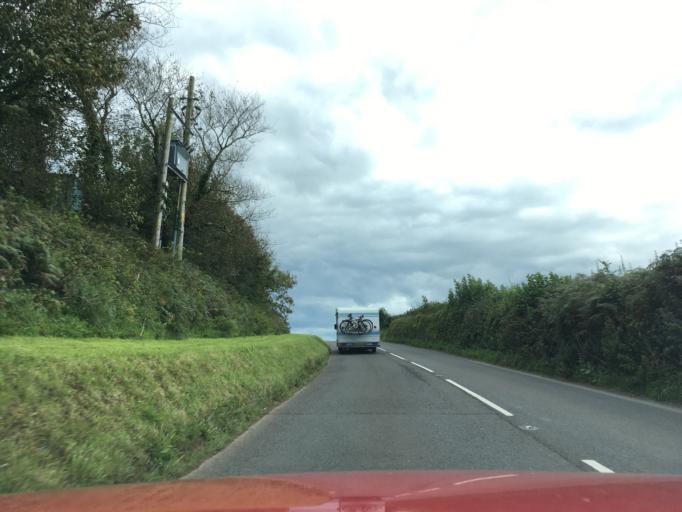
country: GB
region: England
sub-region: Devon
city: Totnes
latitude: 50.3632
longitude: -3.7143
